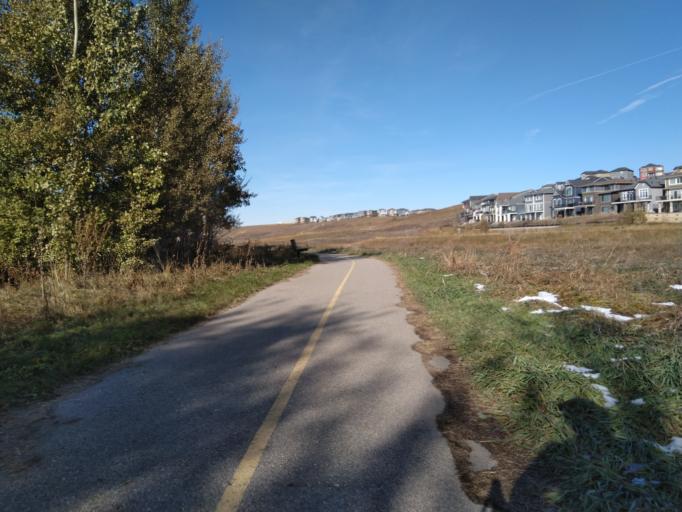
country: CA
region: Alberta
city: Calgary
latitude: 51.1737
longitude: -114.1279
